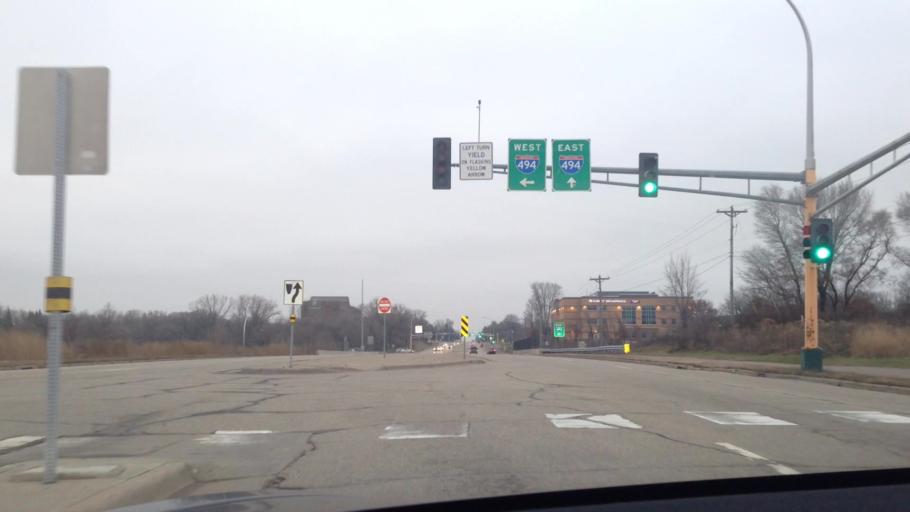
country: US
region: Minnesota
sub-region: Dakota County
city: Mendota Heights
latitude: 44.8627
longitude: -93.1672
